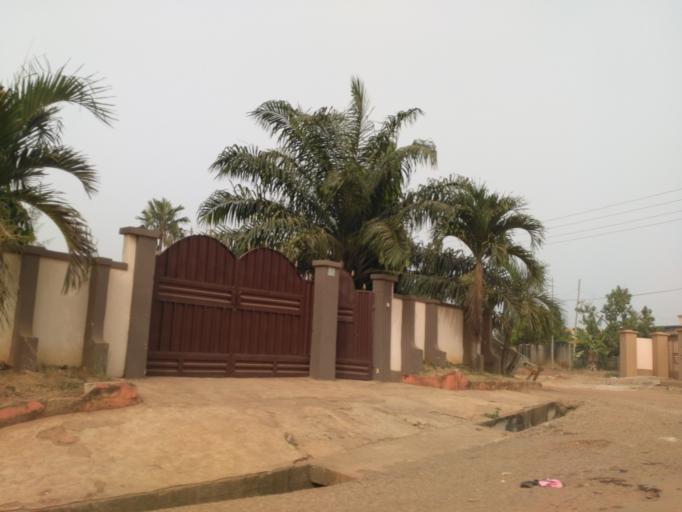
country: GH
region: Ashanti
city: Kumasi
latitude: 6.6422
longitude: -1.6249
